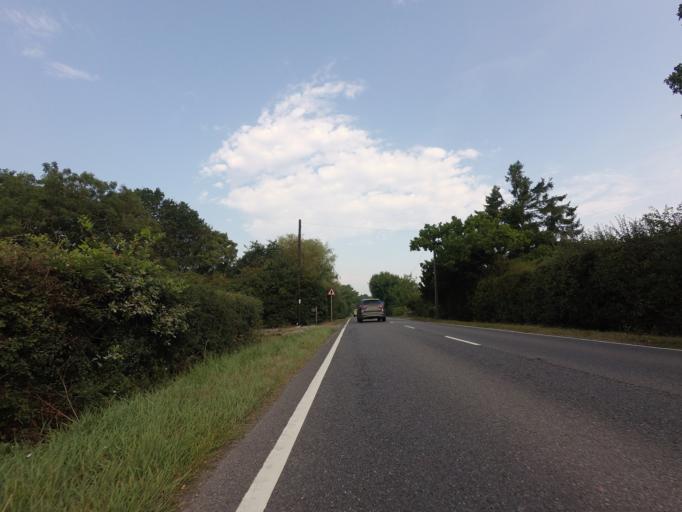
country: GB
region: England
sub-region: Kent
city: Tenterden
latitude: 51.1232
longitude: 0.7660
